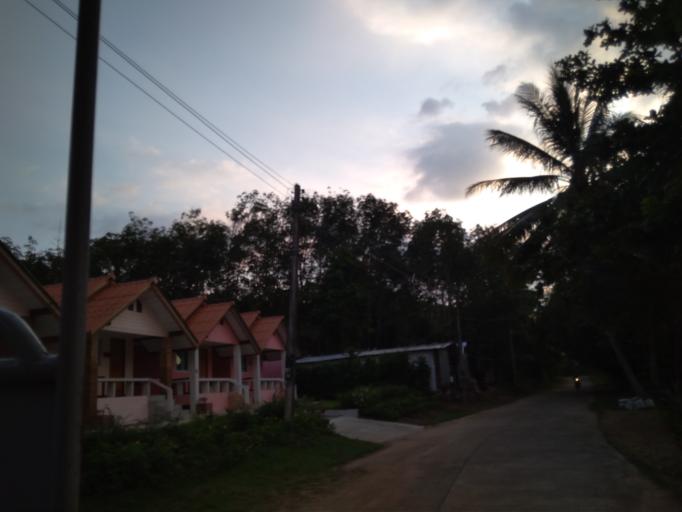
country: TH
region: Phangnga
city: Ko Yao
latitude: 8.1635
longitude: 98.6117
